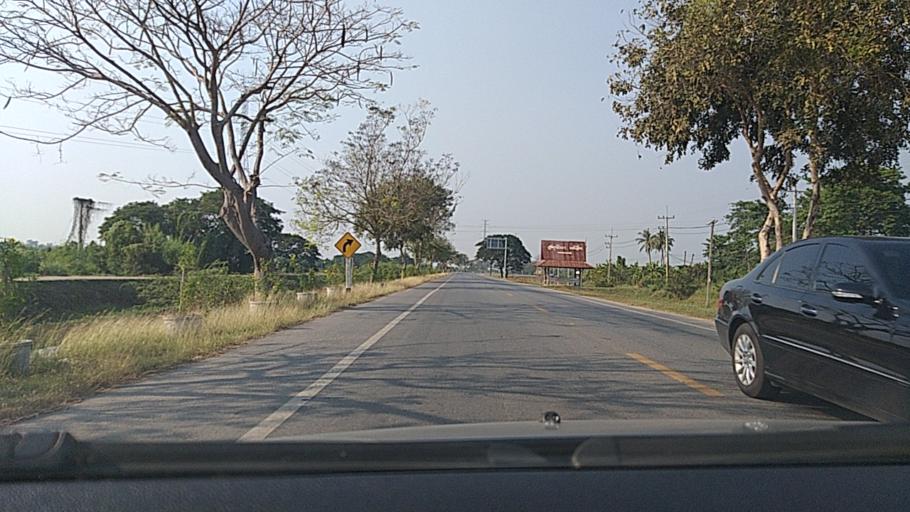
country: TH
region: Ang Thong
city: Chaiyo
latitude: 14.7200
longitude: 100.4319
